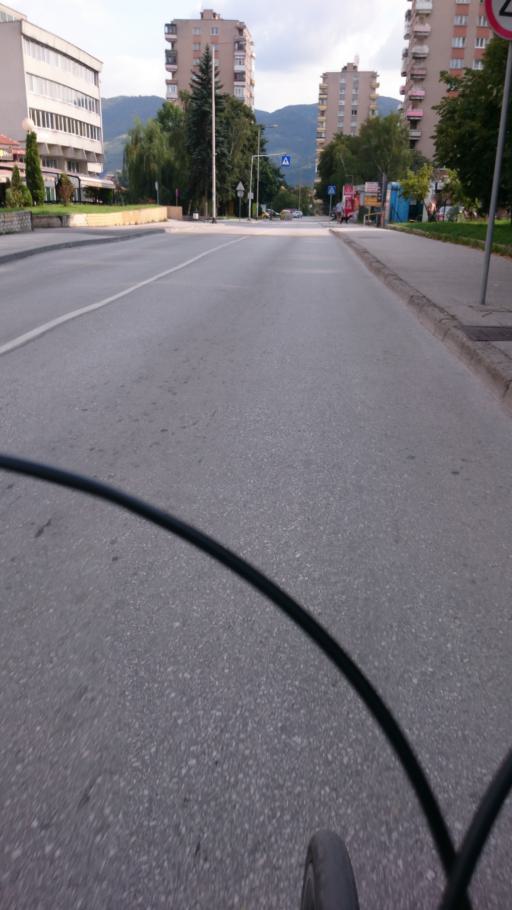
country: BA
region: Federation of Bosnia and Herzegovina
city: Zenica
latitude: 44.2059
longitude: 17.9230
